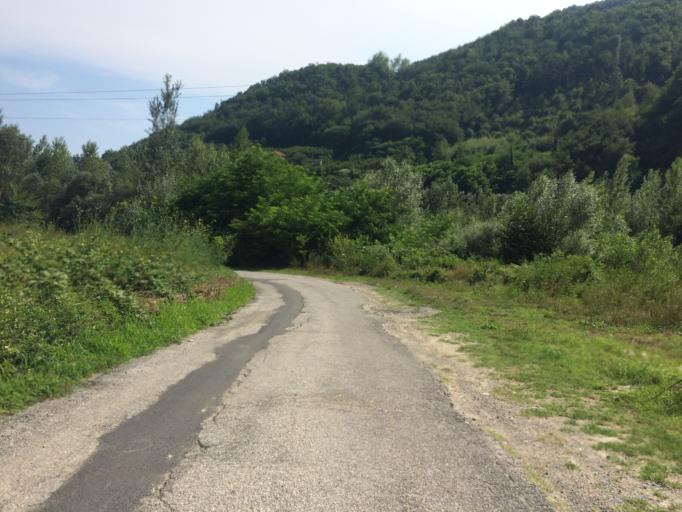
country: IT
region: Piedmont
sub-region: Provincia di Cuneo
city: Cortemilia
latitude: 44.5712
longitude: 8.2023
